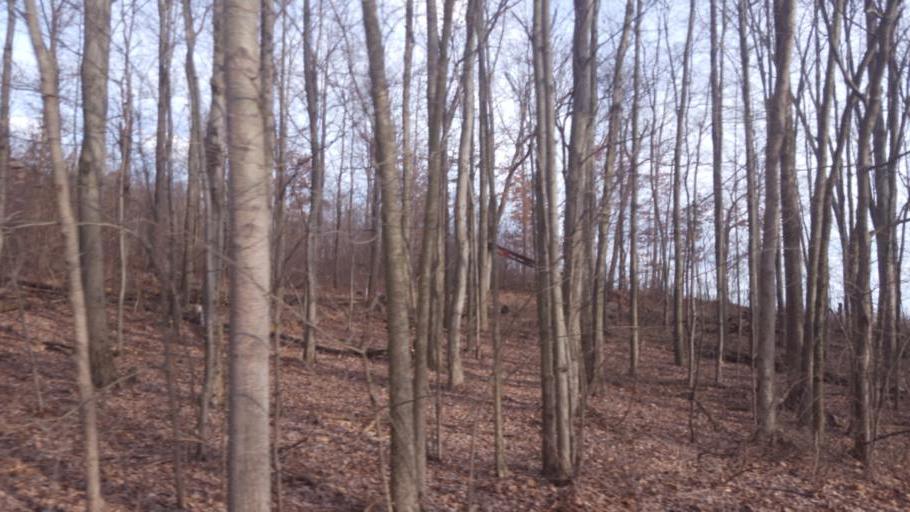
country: US
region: Ohio
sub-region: Ashland County
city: Loudonville
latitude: 40.5725
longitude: -82.3320
